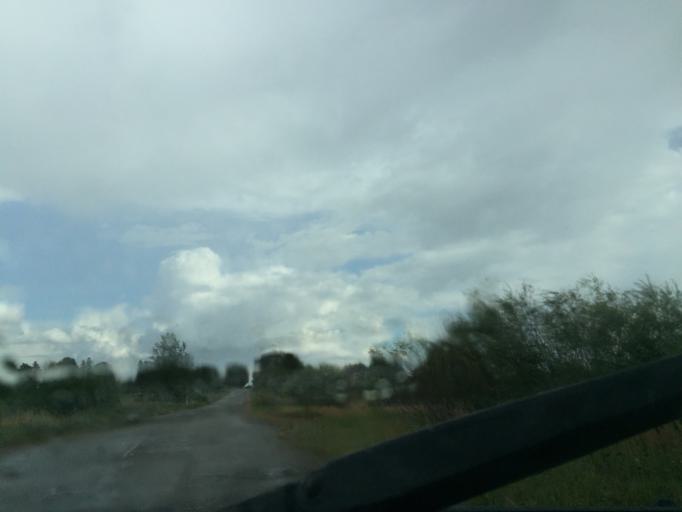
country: LV
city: Tervete
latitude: 56.3672
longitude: 23.4992
